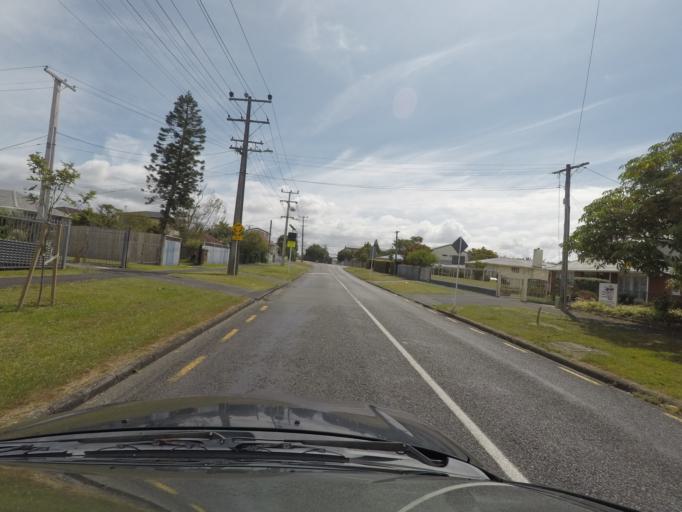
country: NZ
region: Auckland
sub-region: Auckland
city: Waitakere
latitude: -36.9009
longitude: 174.6677
